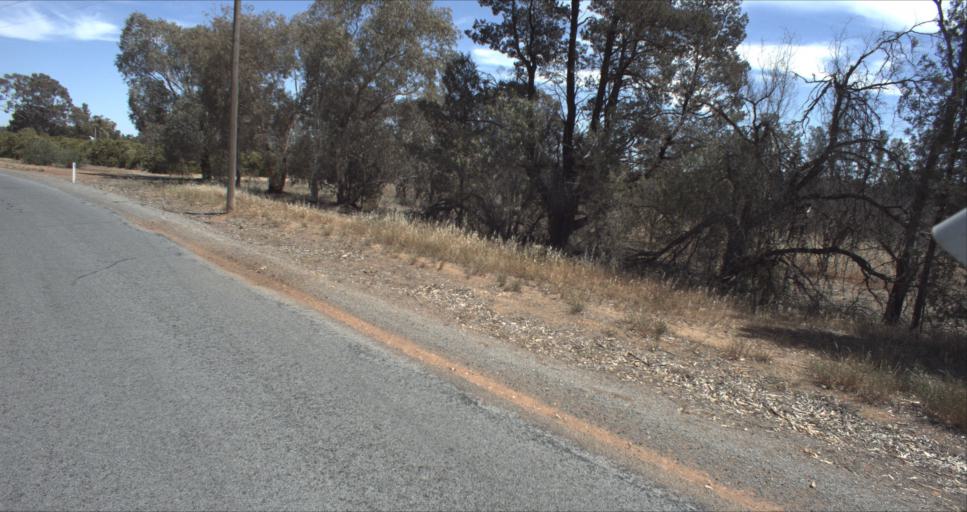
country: AU
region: New South Wales
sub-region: Leeton
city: Leeton
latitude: -34.5727
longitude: 146.4326
